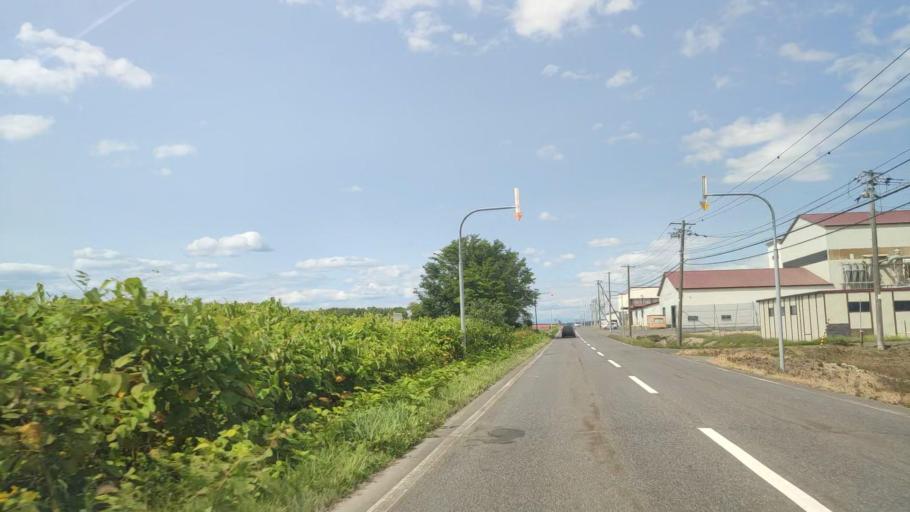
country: JP
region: Hokkaido
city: Nayoro
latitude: 44.2031
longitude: 142.4158
